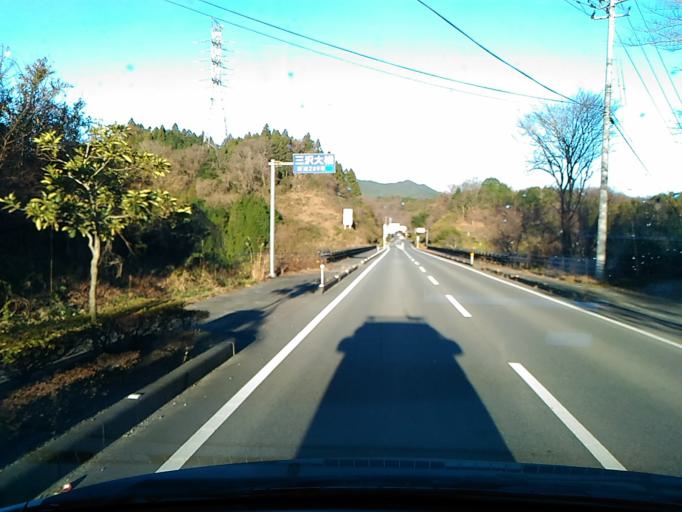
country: JP
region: Ibaraki
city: Kitaibaraki
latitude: 36.9072
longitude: 140.7497
